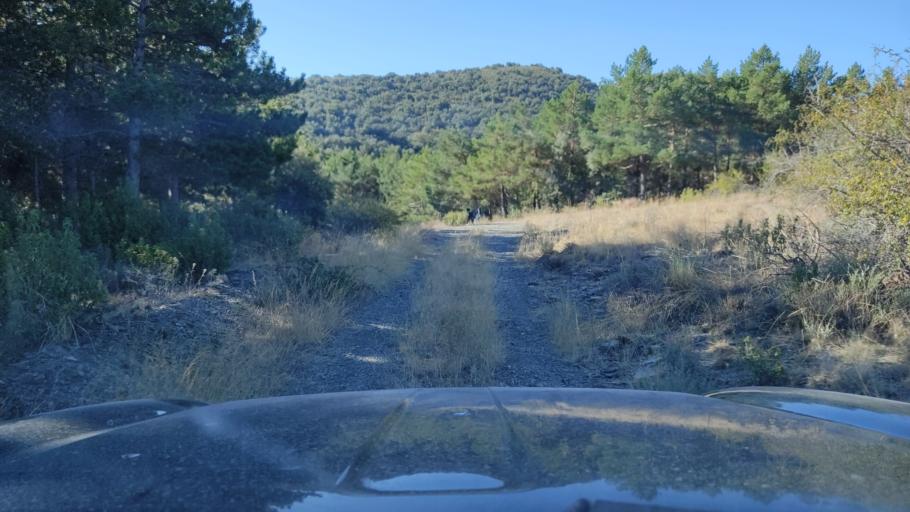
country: ES
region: Aragon
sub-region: Provincia de Teruel
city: Monforte de Moyuela
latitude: 41.0215
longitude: -1.0078
